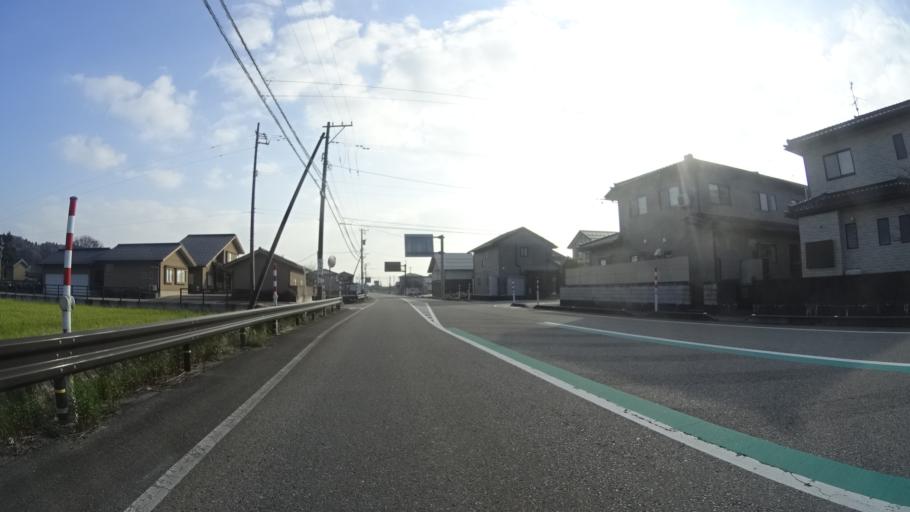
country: JP
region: Toyama
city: Himi
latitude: 36.8768
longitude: 136.9716
